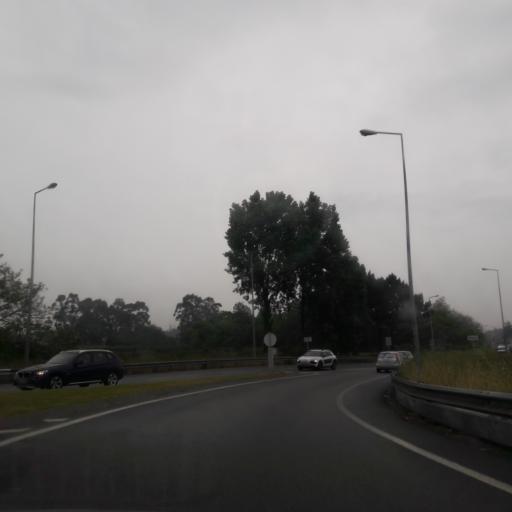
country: PT
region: Porto
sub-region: Vila do Conde
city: Arvore
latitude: 41.3189
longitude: -8.7114
